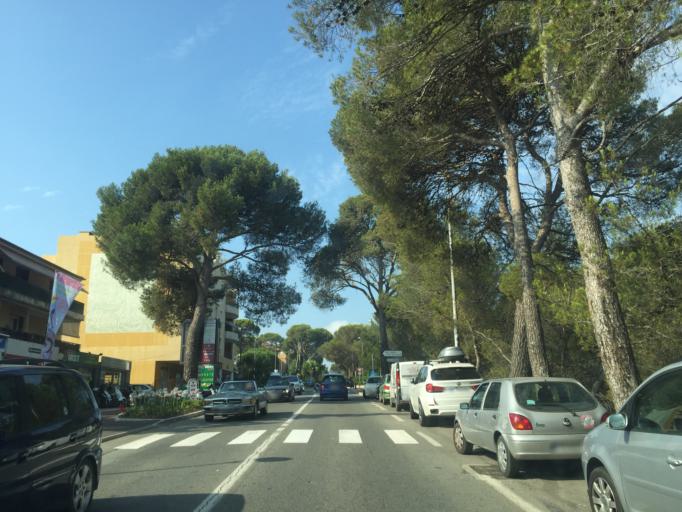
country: FR
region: Provence-Alpes-Cote d'Azur
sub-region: Departement du Var
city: Frejus
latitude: 43.3900
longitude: 6.7257
